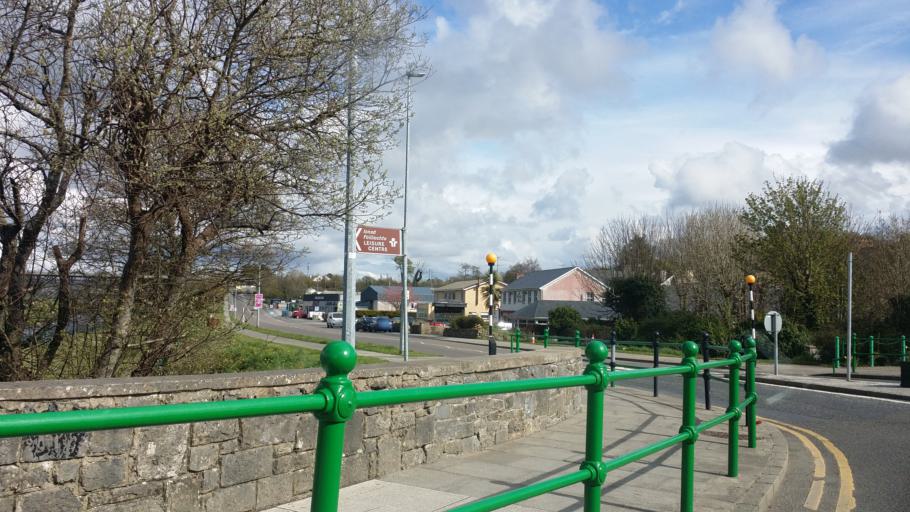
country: IE
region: Ulster
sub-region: County Donegal
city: Ballyshannon
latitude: 54.5005
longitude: -8.1897
